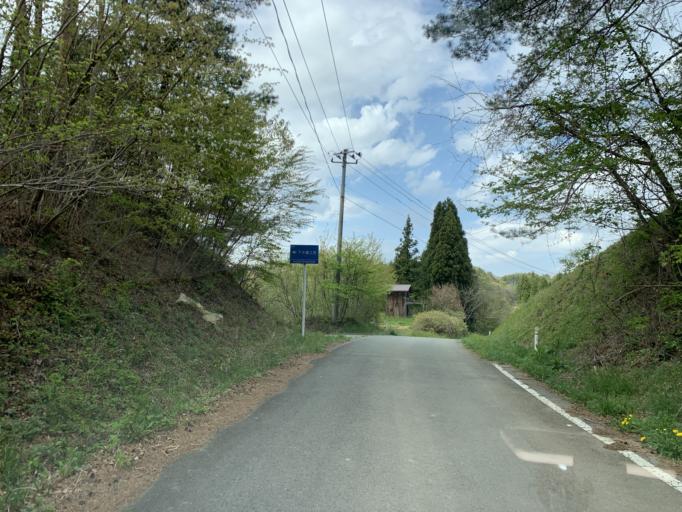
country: JP
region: Iwate
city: Ichinoseki
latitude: 38.7828
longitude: 141.4325
